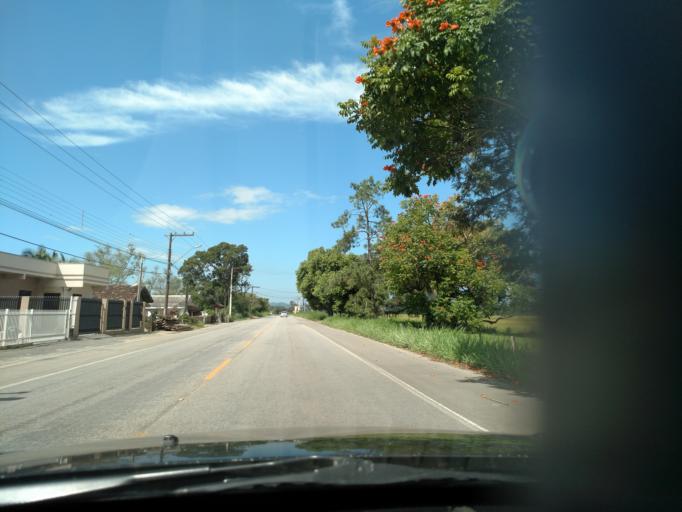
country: BR
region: Santa Catarina
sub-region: Itajai
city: Itajai
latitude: -26.8861
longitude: -48.8086
